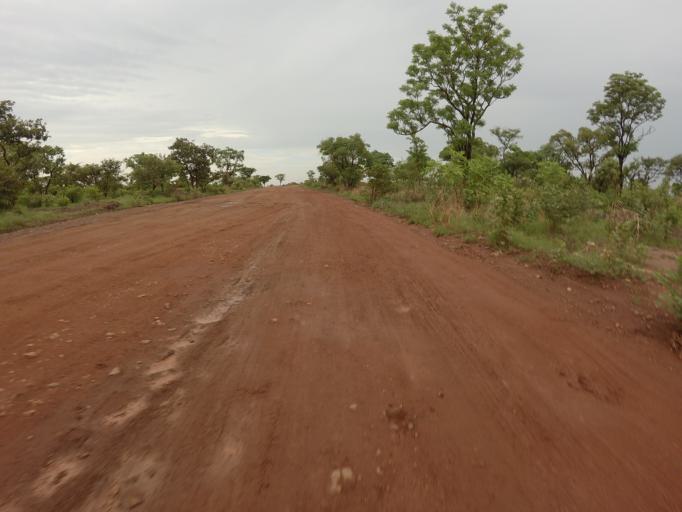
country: GH
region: Upper East
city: Bolgatanga
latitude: 10.8781
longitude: -0.6287
